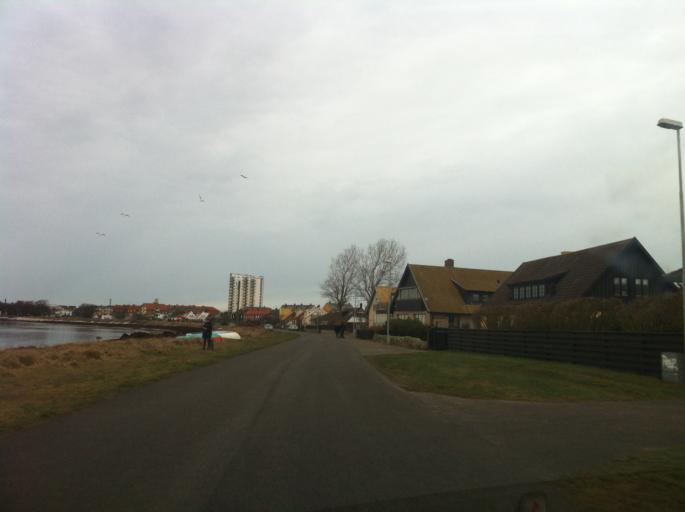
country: SE
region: Skane
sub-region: Hoganas Kommun
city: Hoganas
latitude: 56.1943
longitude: 12.5547
